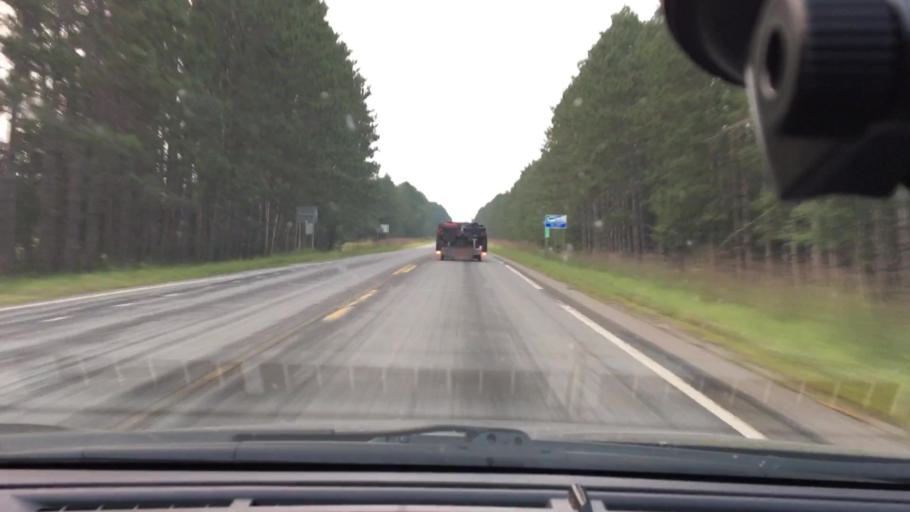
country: US
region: Minnesota
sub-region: Crow Wing County
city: Cross Lake
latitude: 46.7608
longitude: -93.9665
